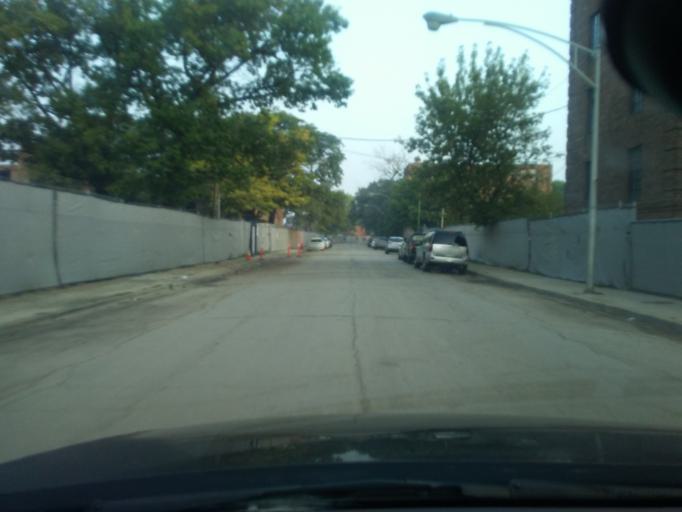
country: US
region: Illinois
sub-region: Cook County
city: Lincolnwood
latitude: 41.9328
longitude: -87.6813
